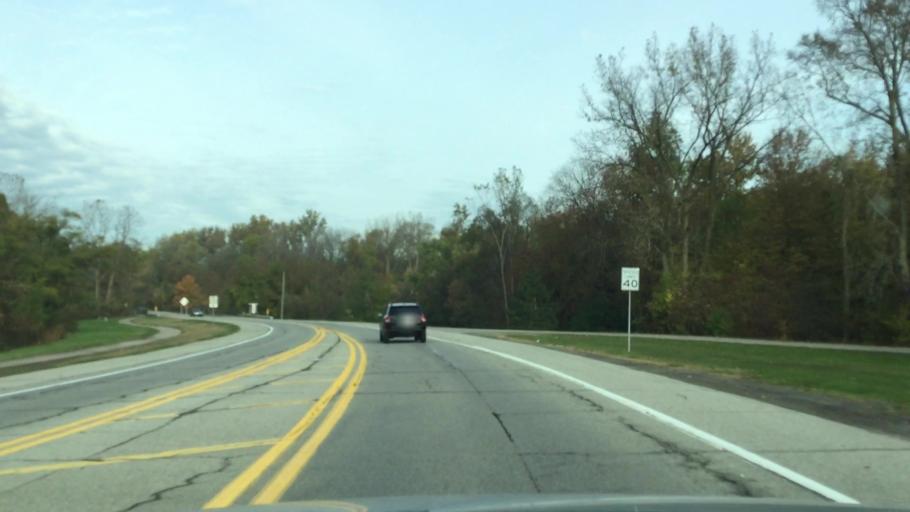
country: US
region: Michigan
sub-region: Wayne County
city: Dearborn Heights
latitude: 42.3296
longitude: -83.2457
